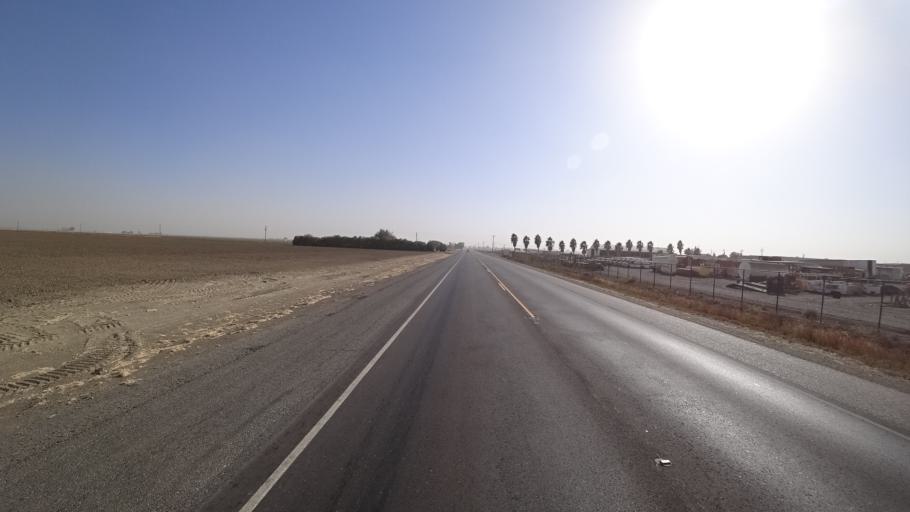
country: US
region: California
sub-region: Yolo County
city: Woodland
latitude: 38.7508
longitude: -121.7293
